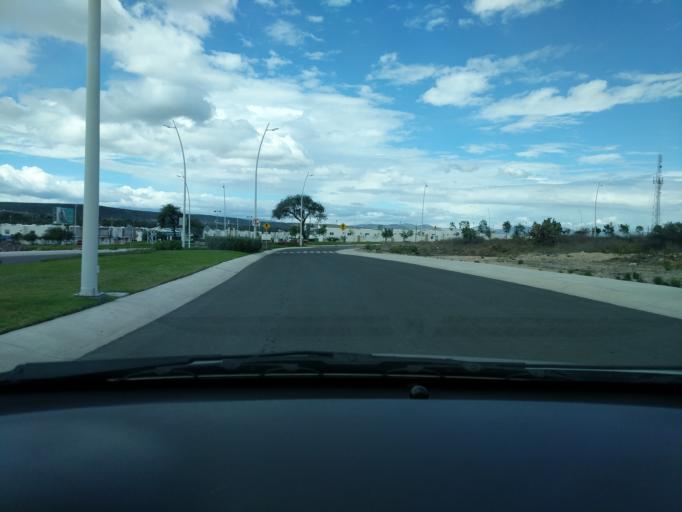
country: MX
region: Queretaro
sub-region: El Marques
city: El Pozo
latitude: 20.6459
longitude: -100.3117
